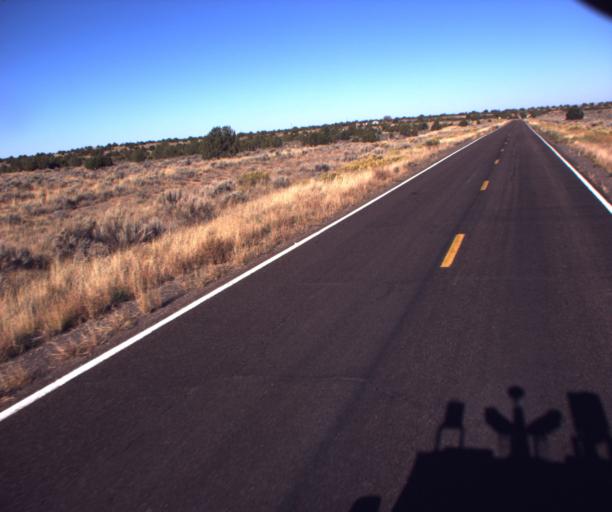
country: US
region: Arizona
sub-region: Navajo County
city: First Mesa
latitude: 35.7991
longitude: -110.1940
